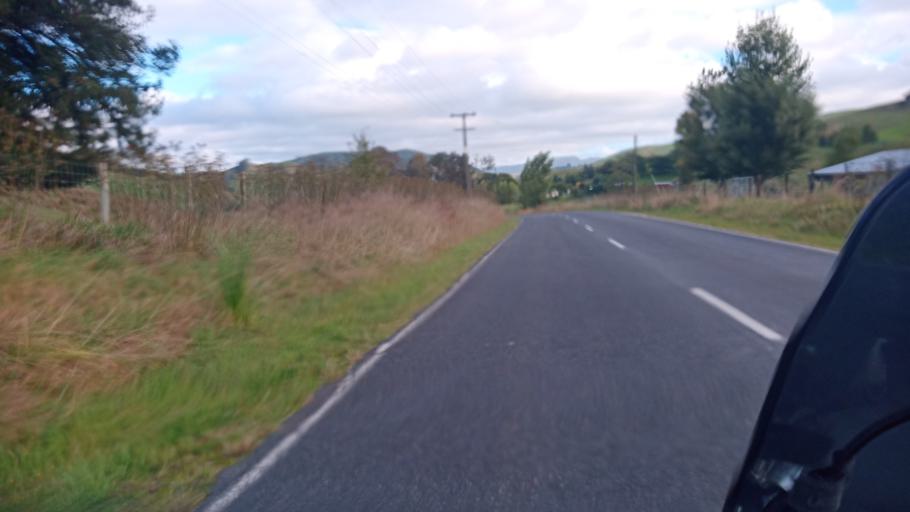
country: NZ
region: Gisborne
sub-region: Gisborne District
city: Gisborne
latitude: -38.5840
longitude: 177.7526
